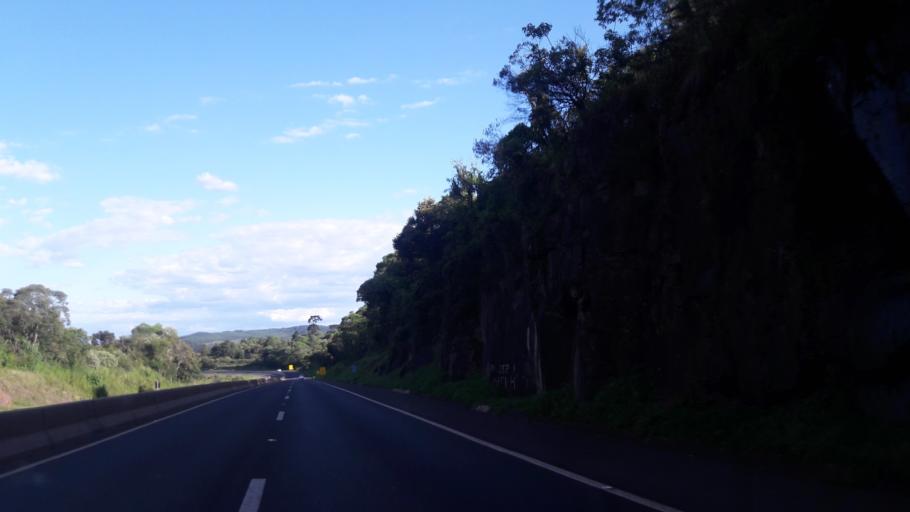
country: BR
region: Parana
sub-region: Guarapuava
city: Guarapuava
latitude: -25.3505
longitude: -51.3776
